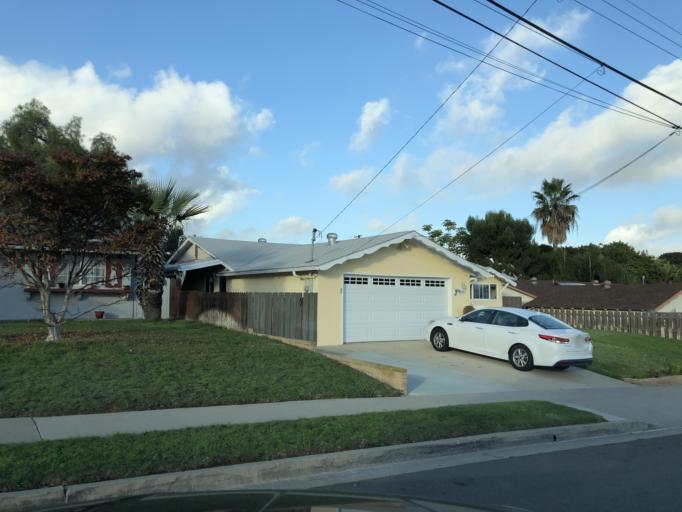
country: US
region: California
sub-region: San Diego County
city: San Diego
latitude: 32.8178
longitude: -117.1732
